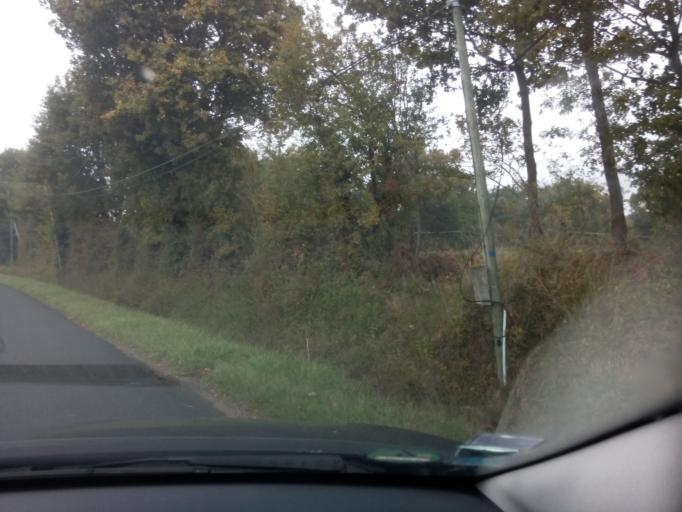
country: FR
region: Pays de la Loire
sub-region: Departement de Maine-et-Loire
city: Soulaire-et-Bourg
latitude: 47.6166
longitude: -0.5419
